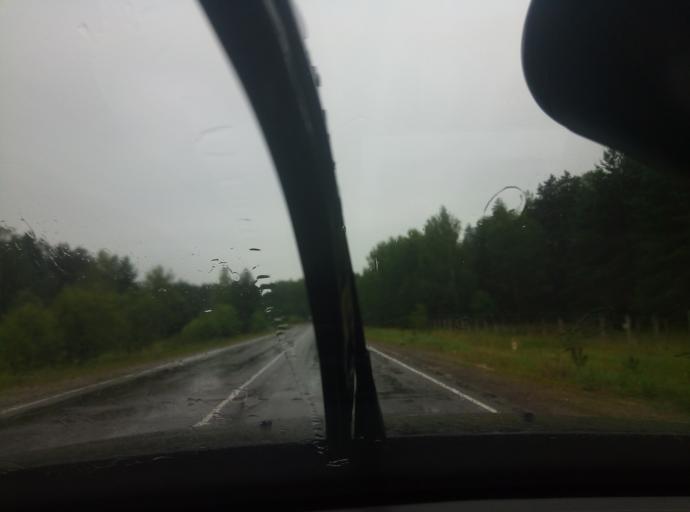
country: RU
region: Kaluga
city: Kremenki
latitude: 54.8769
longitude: 37.1459
